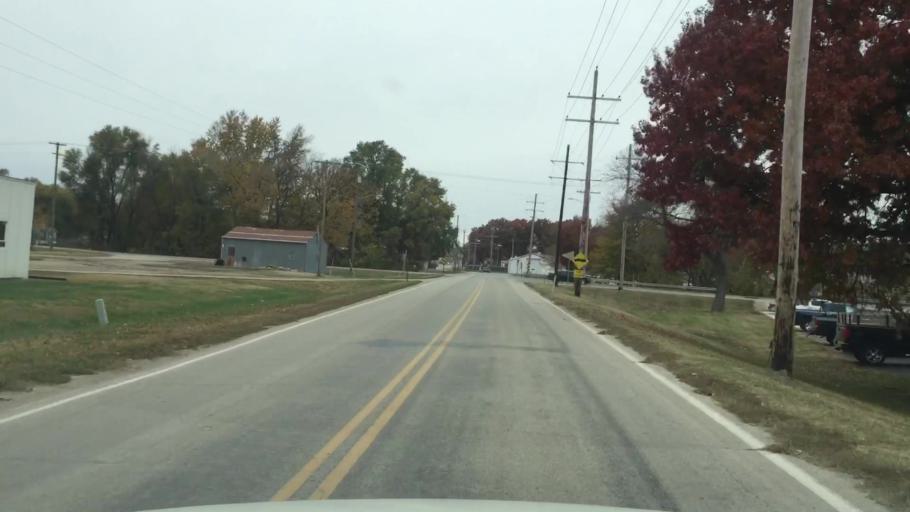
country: US
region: Kansas
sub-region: Pottawatomie County
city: Wamego
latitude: 39.2031
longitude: -96.2945
